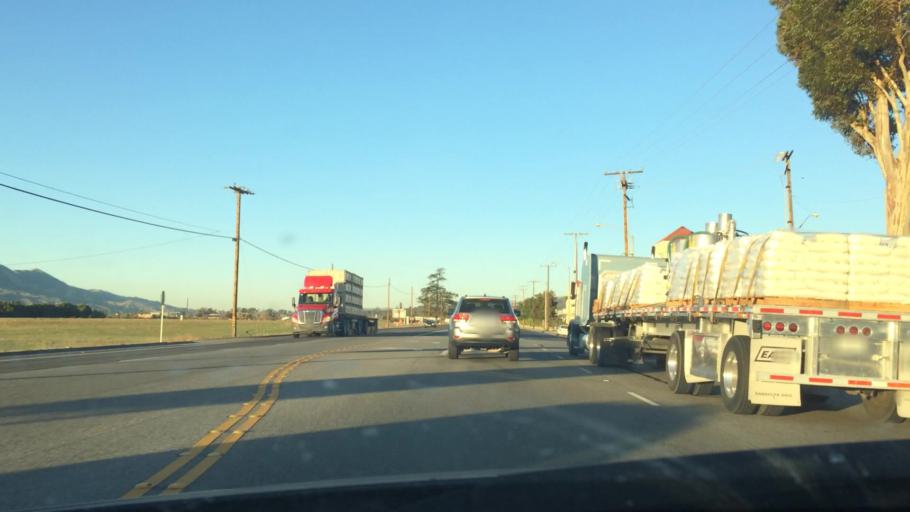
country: US
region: California
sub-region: Ventura County
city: Fillmore
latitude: 34.3944
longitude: -118.9314
